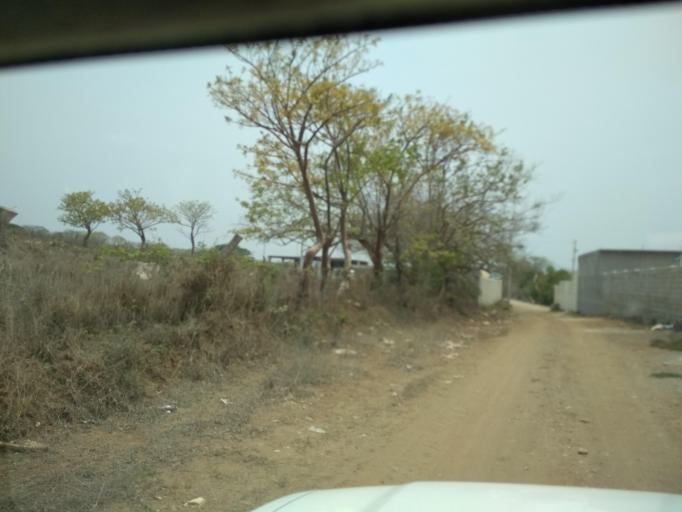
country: MX
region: Veracruz
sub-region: Veracruz
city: Delfino Victoria (Santa Fe)
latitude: 19.2213
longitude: -96.2611
